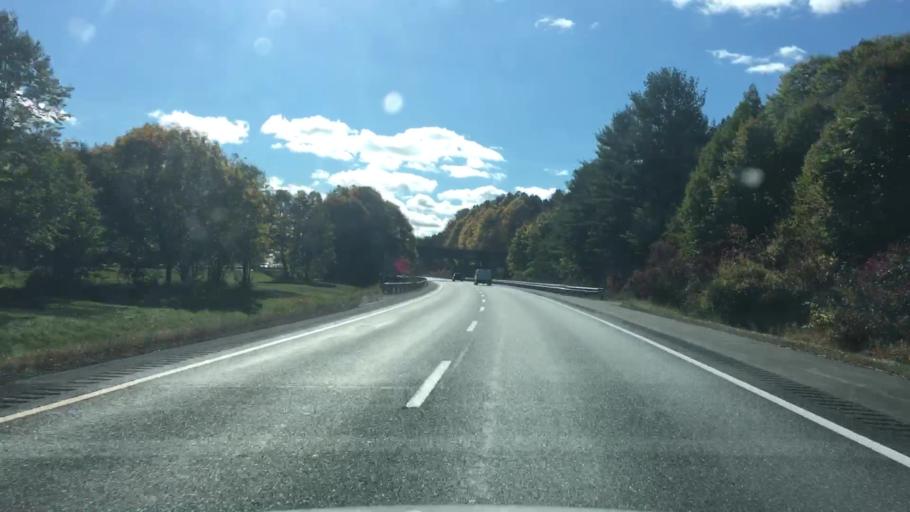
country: US
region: Maine
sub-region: Kennebec County
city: Waterville
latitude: 44.5675
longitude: -69.6685
